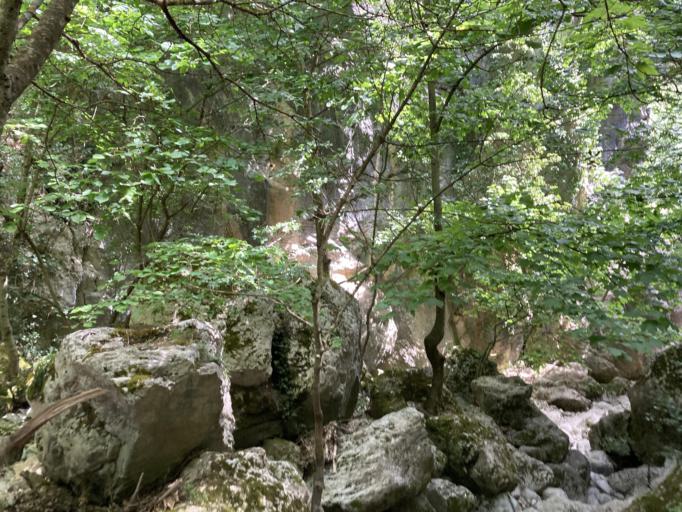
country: IT
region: Abruzzo
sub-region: Provincia dell' Aquila
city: Aielli
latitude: 42.0895
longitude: 13.5691
